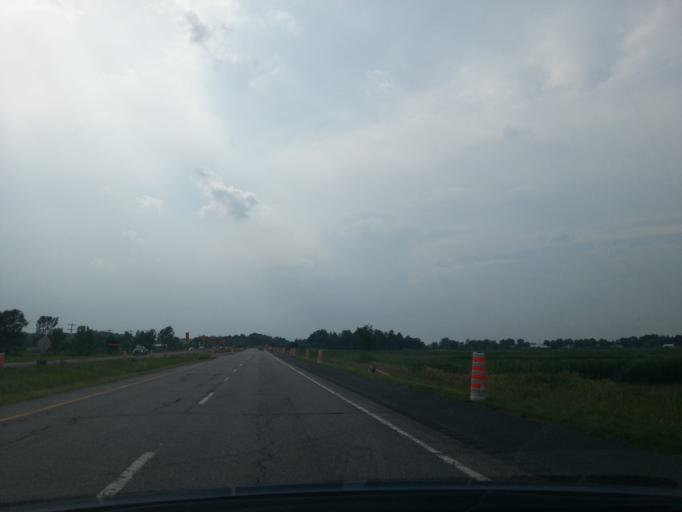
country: CA
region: Quebec
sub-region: Monteregie
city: Rigaud
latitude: 45.4730
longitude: -74.2685
